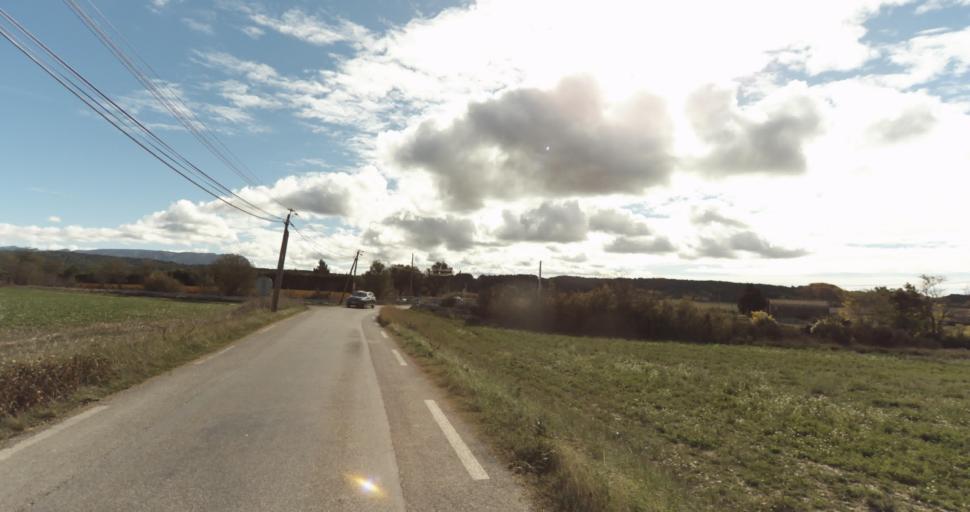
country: FR
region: Provence-Alpes-Cote d'Azur
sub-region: Departement des Bouches-du-Rhone
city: Venelles
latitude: 43.5871
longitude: 5.4888
